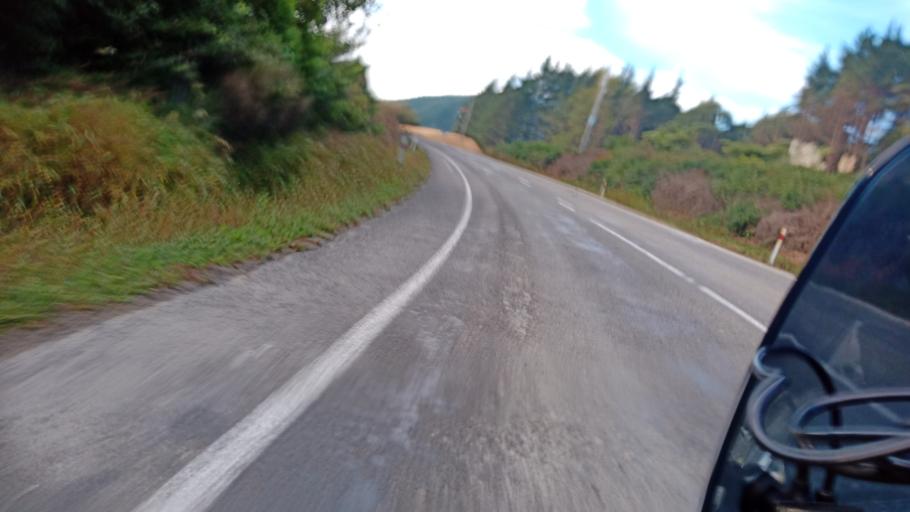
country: NZ
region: Gisborne
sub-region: Gisborne District
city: Gisborne
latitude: -38.8358
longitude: 177.8947
